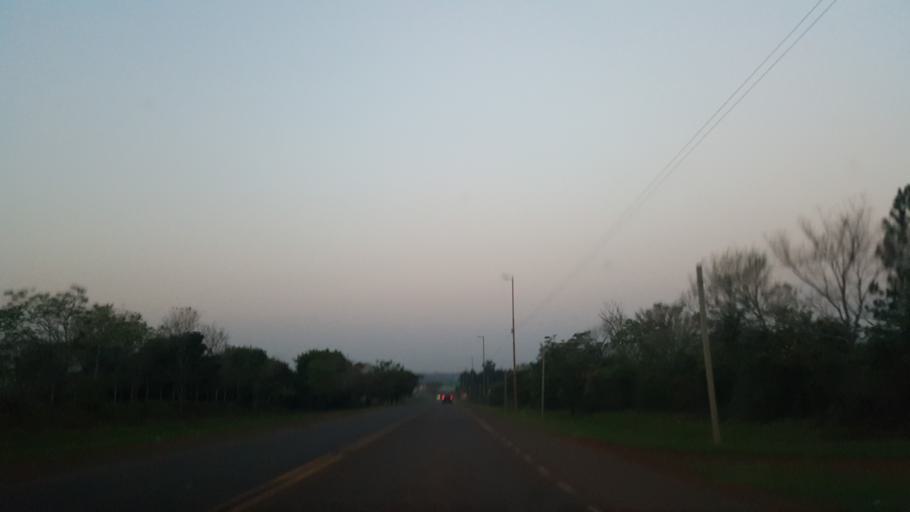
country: AR
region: Misiones
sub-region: Departamento de Capital
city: Posadas
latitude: -27.4044
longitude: -55.9701
